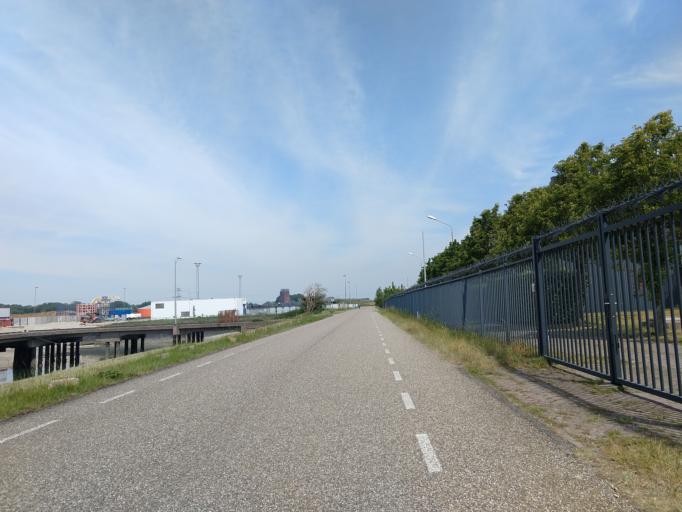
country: NL
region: Zeeland
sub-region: Gemeente Vlissingen
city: Vlissingen
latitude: 51.4510
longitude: 3.6011
